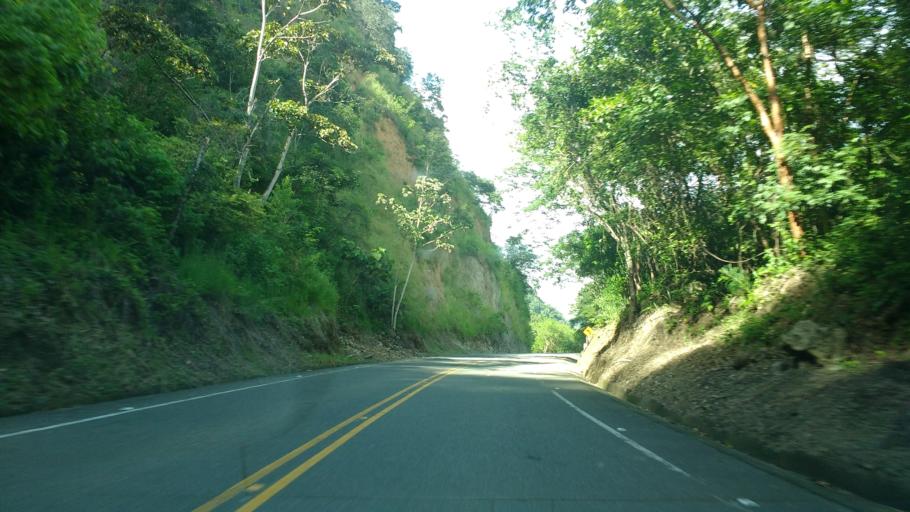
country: CO
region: Antioquia
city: Concordia
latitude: 6.0737
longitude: -75.8615
